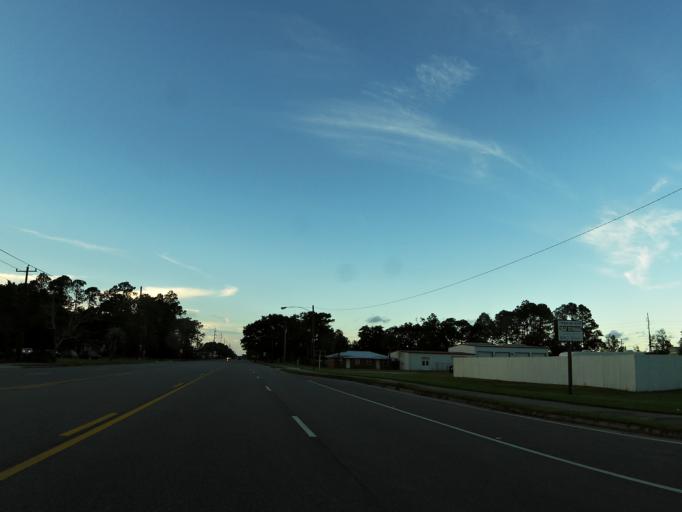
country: US
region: Georgia
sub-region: Camden County
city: St Marys
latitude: 30.7637
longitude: -81.5764
